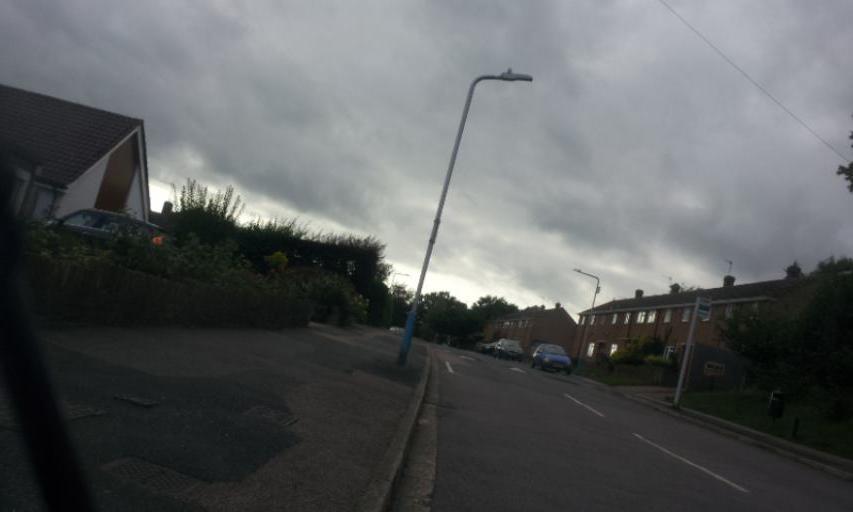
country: GB
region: England
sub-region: Kent
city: Tonbridge
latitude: 51.2093
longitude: 0.2925
